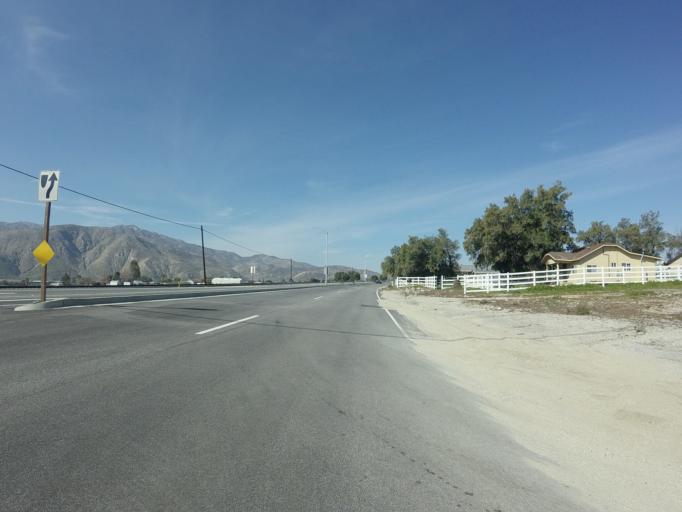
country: US
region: California
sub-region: Riverside County
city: Cabazon
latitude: 33.9160
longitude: -116.7875
